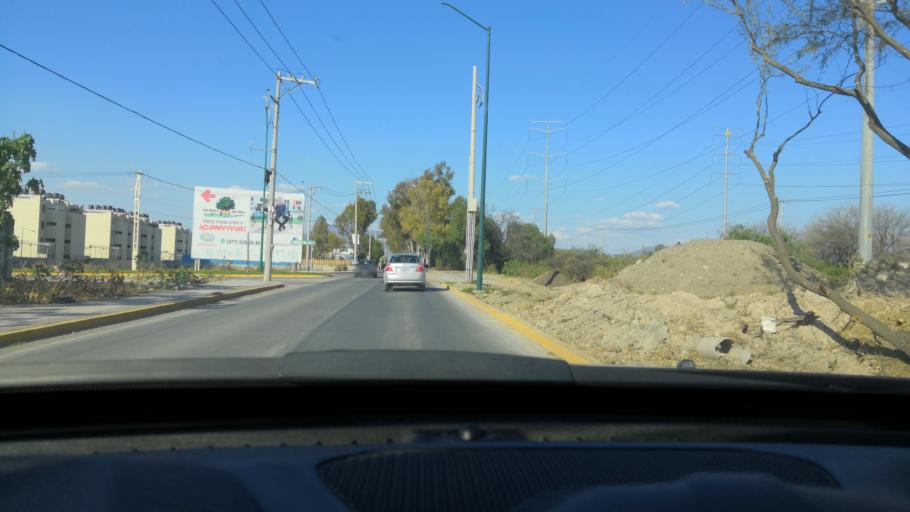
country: MX
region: Guanajuato
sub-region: Leon
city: Fraccionamiento Paraiso Real
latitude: 21.0632
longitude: -101.6068
